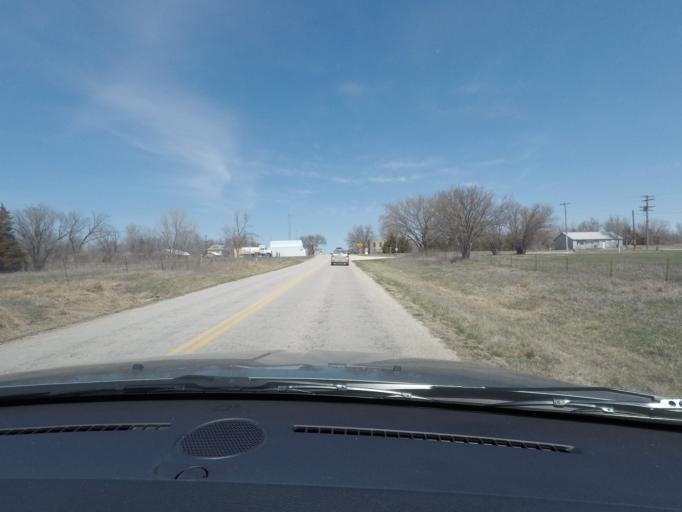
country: US
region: Kansas
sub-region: Lyon County
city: Emporia
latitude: 38.6531
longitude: -96.1698
